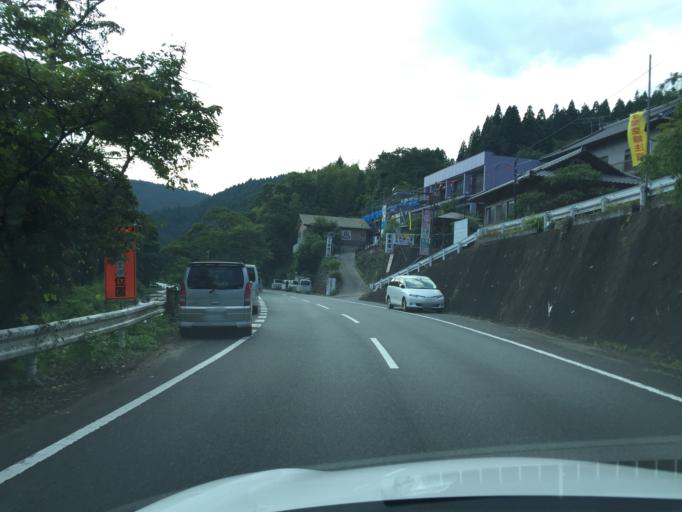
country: JP
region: Fukushima
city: Iwaki
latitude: 37.0096
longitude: 140.7172
